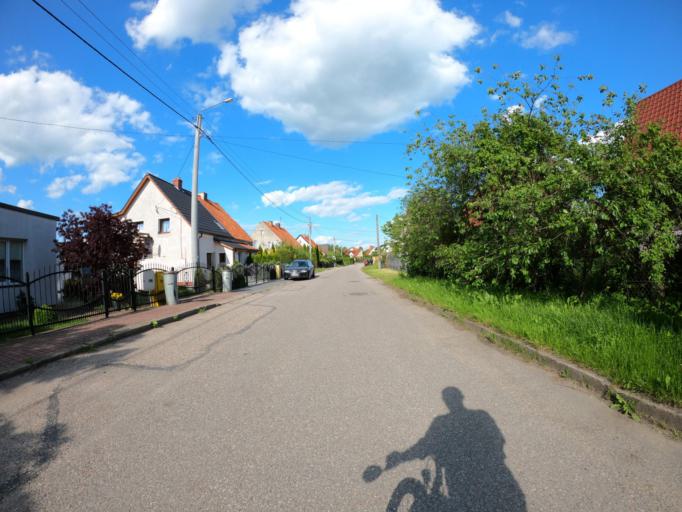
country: PL
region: Warmian-Masurian Voivodeship
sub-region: Powiat lidzbarski
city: Lidzbark Warminski
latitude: 54.1314
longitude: 20.5960
